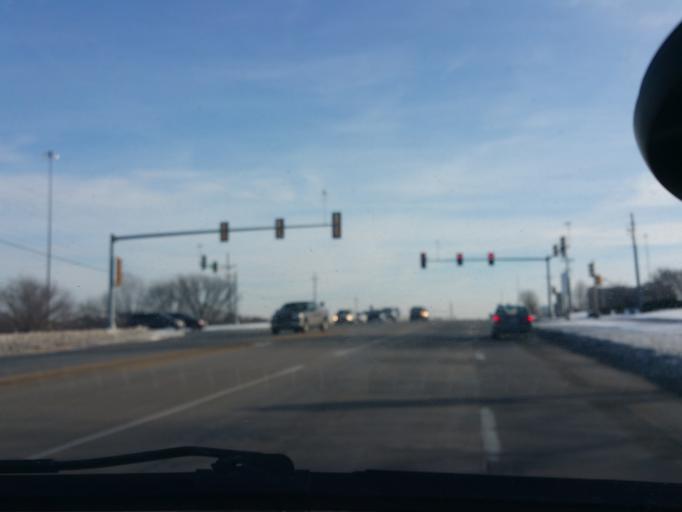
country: US
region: Iowa
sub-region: Polk County
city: Clive
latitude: 41.6004
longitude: -93.7801
